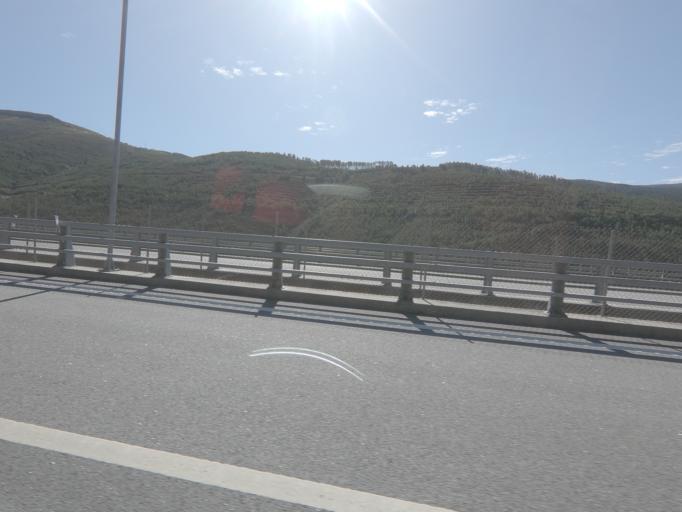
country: PT
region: Guarda
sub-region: Sabugal
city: Sabugal
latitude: 40.4147
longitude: -6.9388
